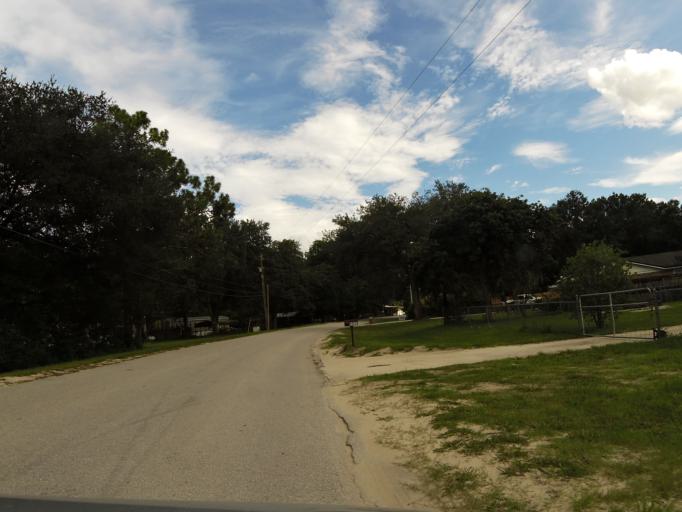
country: US
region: Florida
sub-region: Clay County
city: Green Cove Springs
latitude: 29.9873
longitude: -81.7190
